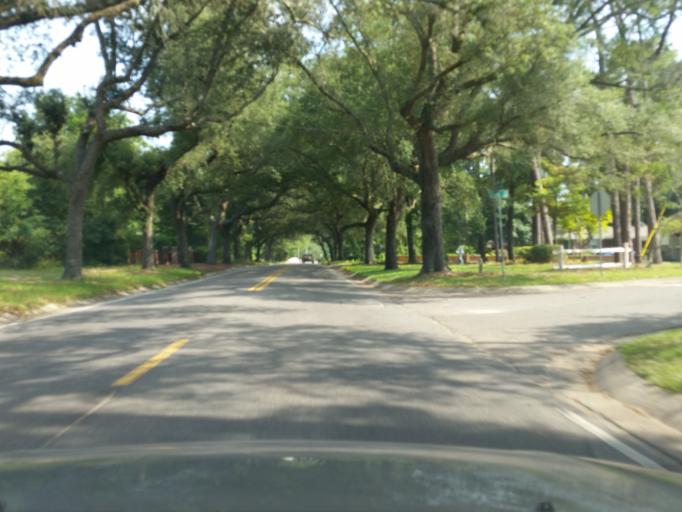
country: US
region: Florida
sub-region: Escambia County
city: Goulding
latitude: 30.4550
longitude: -87.2098
